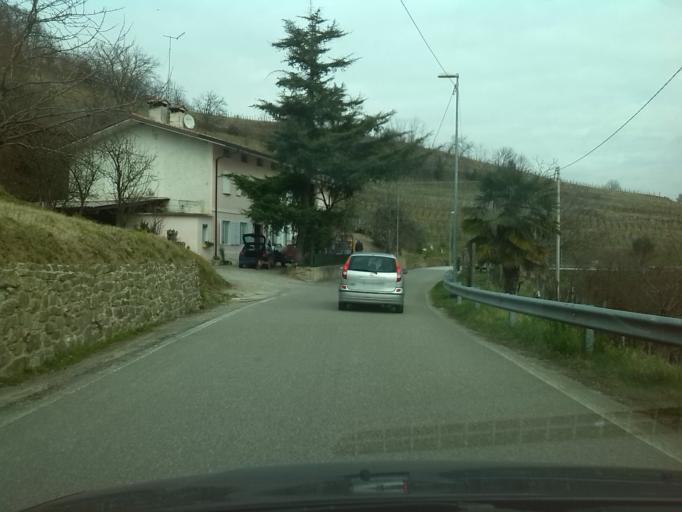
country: IT
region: Friuli Venezia Giulia
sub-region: Provincia di Gorizia
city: San Floriano del Collio
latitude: 45.9701
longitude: 13.5821
